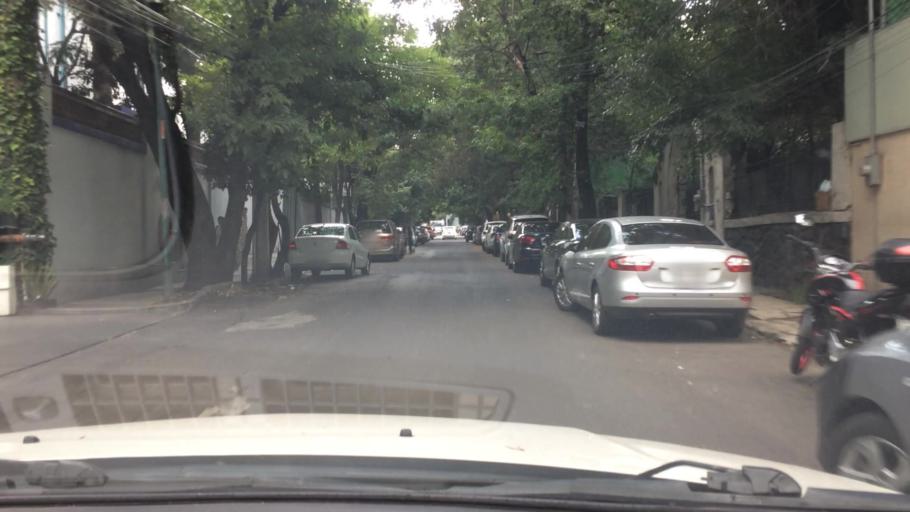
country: MX
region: Mexico City
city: Alvaro Obregon
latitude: 19.3506
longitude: -99.1885
